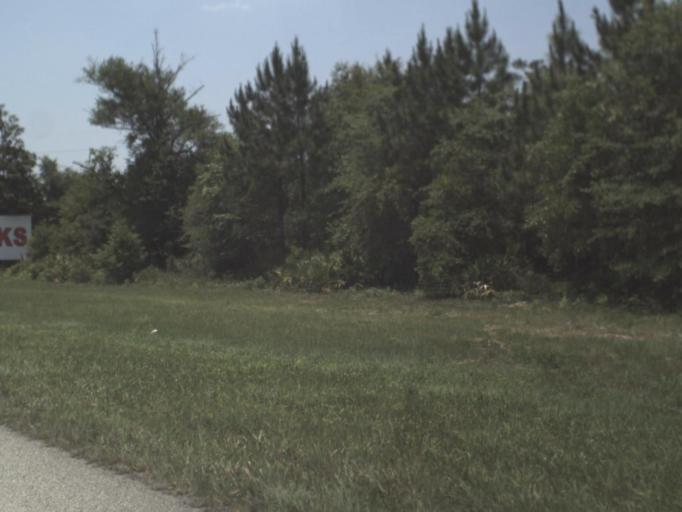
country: US
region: Florida
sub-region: Bradford County
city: Starke
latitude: 30.1055
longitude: -82.0515
